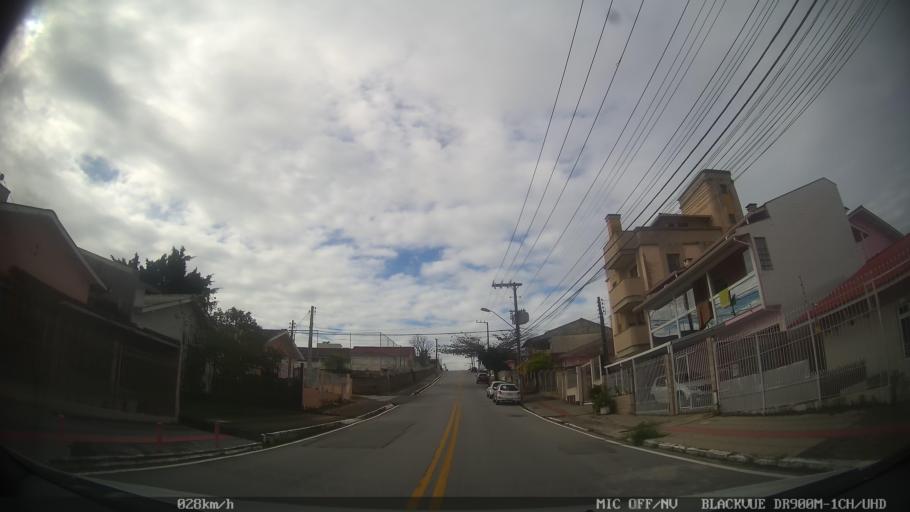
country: BR
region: Santa Catarina
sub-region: Sao Jose
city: Campinas
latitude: -27.5733
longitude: -48.6204
